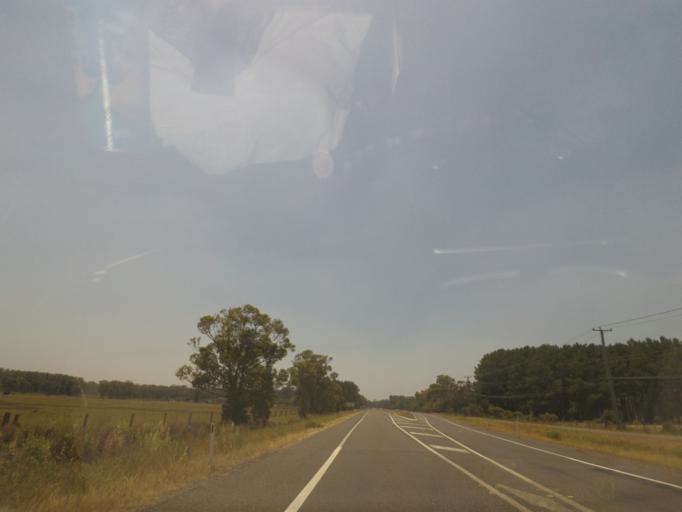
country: AU
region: New South Wales
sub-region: Port Stephens Shire
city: Medowie
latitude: -32.7941
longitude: 151.8954
